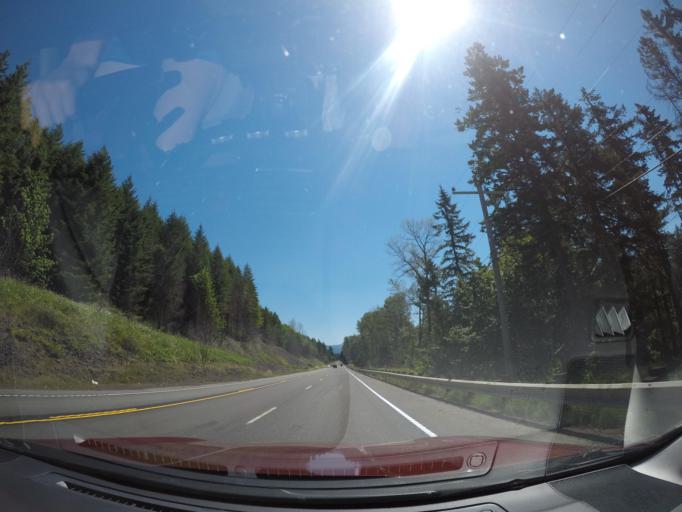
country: US
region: Oregon
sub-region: Linn County
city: Mill City
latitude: 44.7563
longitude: -122.4568
